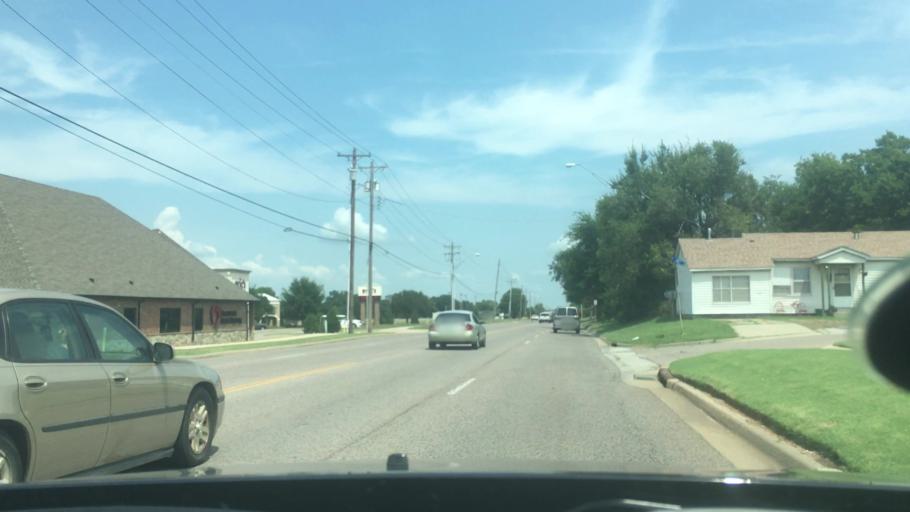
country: US
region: Oklahoma
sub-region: Pottawatomie County
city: Shawnee
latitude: 35.3654
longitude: -96.9297
